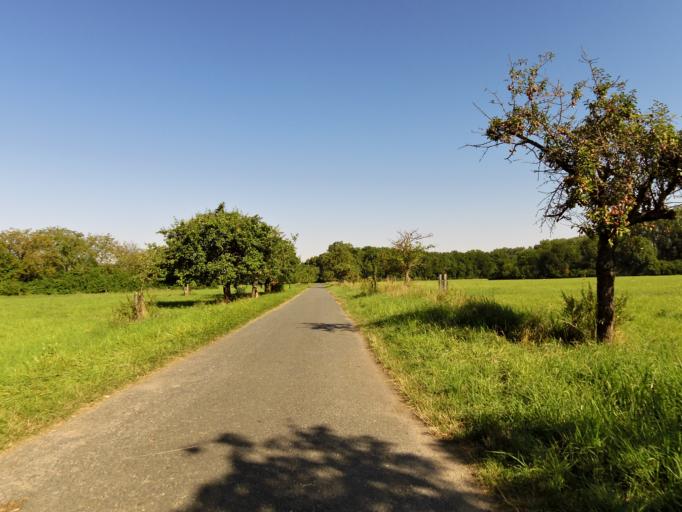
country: DE
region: Hesse
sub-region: Regierungsbezirk Darmstadt
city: Stockstadt am Rhein
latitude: 49.8178
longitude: 8.4578
